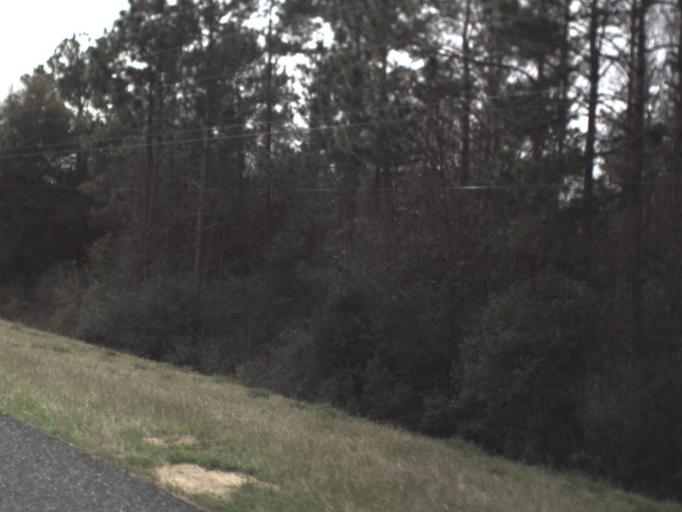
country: US
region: Florida
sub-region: Bay County
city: Youngstown
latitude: 30.5213
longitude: -85.4081
